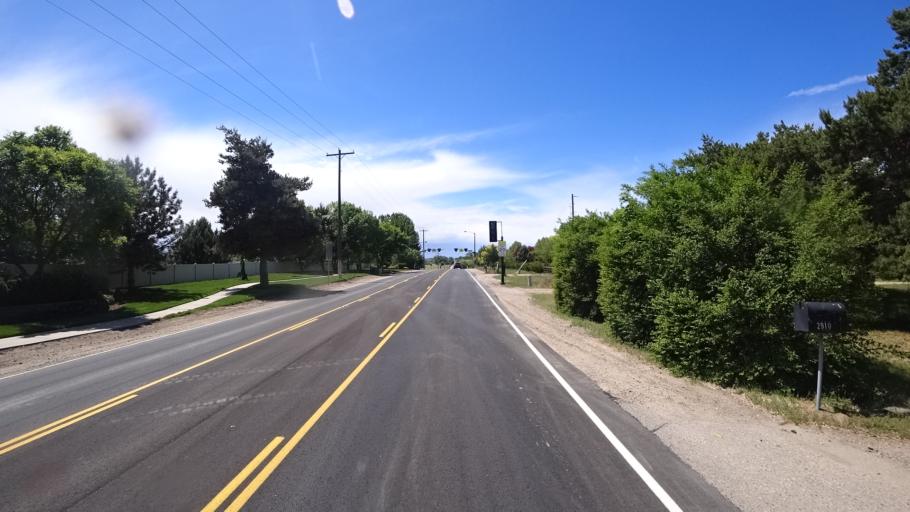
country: US
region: Idaho
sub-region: Ada County
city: Meridian
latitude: 43.5757
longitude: -116.3583
